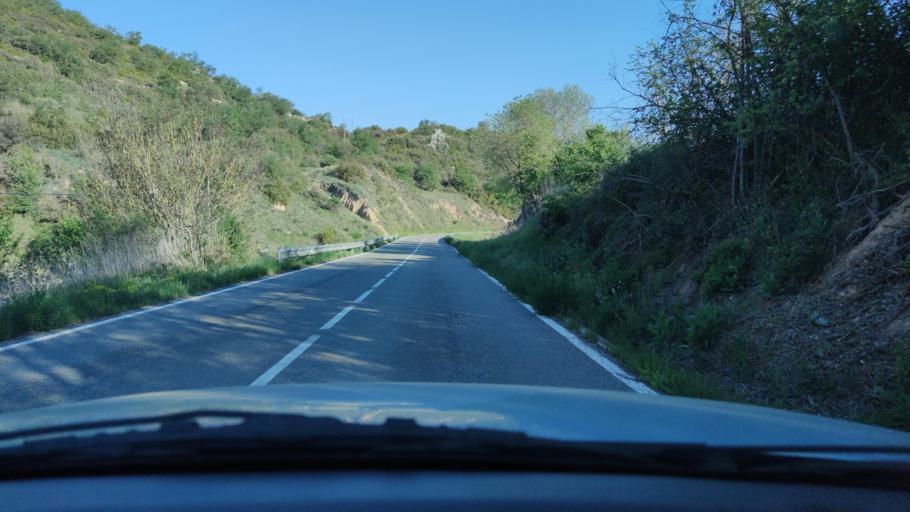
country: ES
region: Catalonia
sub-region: Provincia de Lleida
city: Artesa de Segre
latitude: 41.8840
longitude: 0.9993
